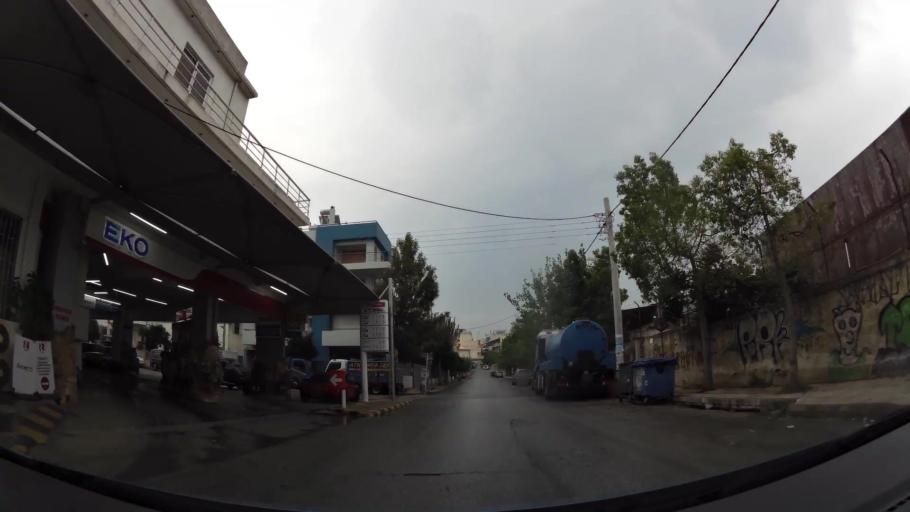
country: GR
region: Attica
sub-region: Nomarchia Athinas
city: Ymittos
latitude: 37.9523
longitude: 23.7456
